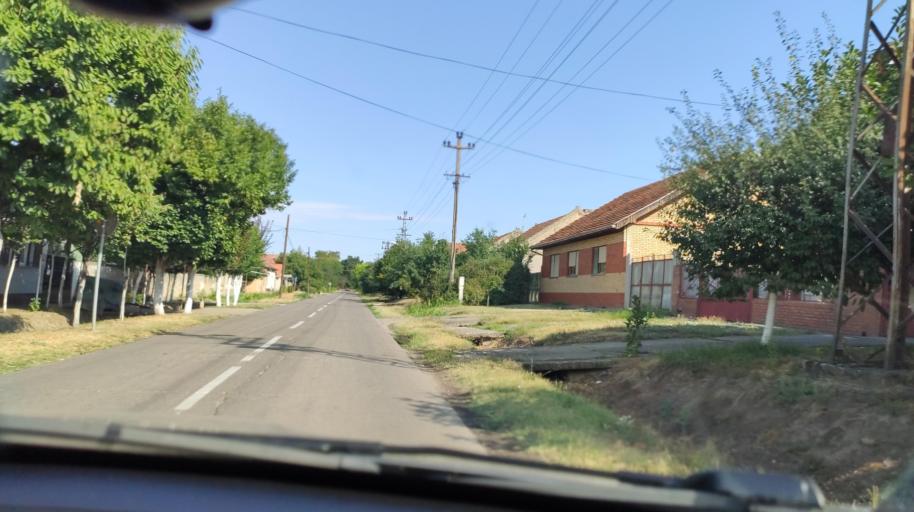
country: RS
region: Autonomna Pokrajina Vojvodina
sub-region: Severnobacki Okrug
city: Backa Topola
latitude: 45.8067
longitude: 19.6259
